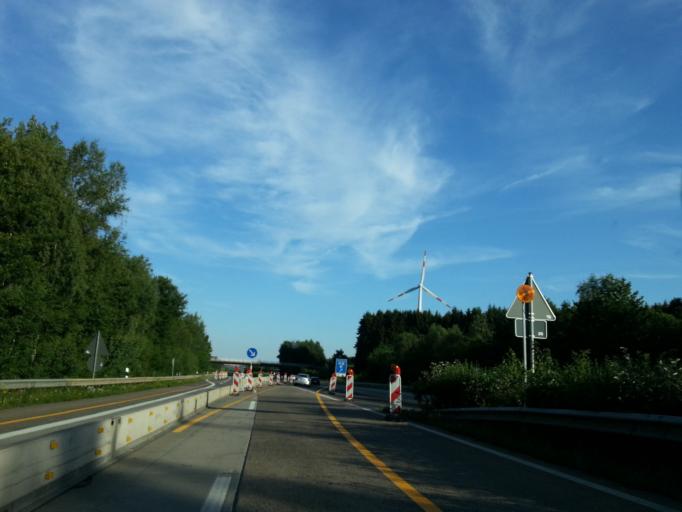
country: DE
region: Rheinland-Pfalz
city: Hinzert-Polert
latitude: 49.6949
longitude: 6.8921
